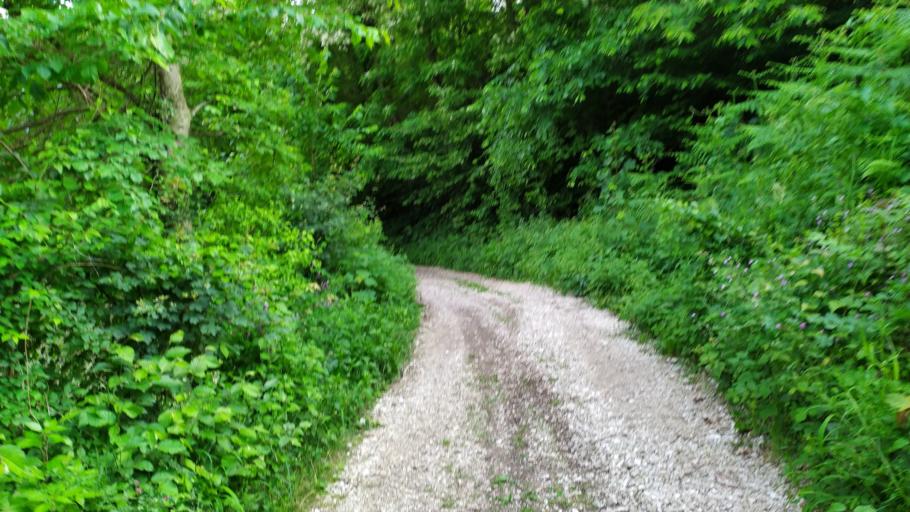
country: IT
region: Veneto
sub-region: Provincia di Vicenza
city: Torrebelvicino
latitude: 45.6884
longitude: 11.3116
